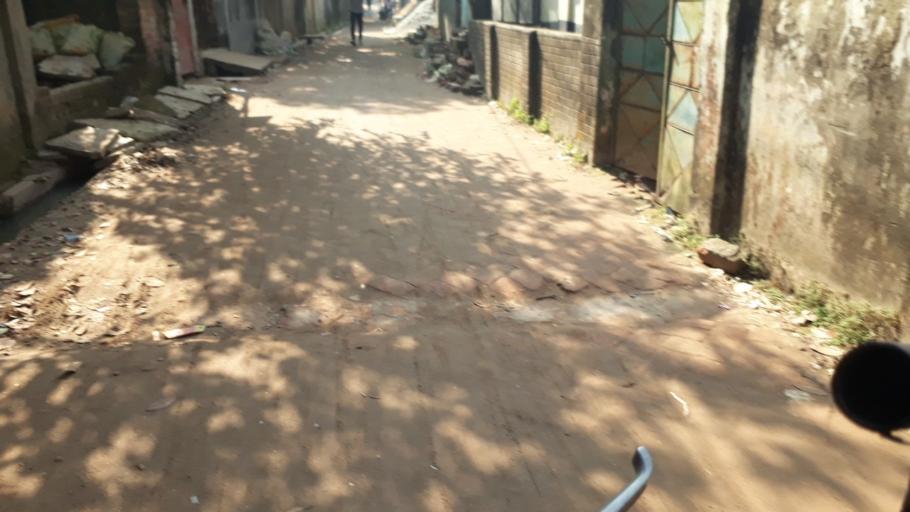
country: BD
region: Dhaka
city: Tungi
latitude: 23.8599
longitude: 90.2613
